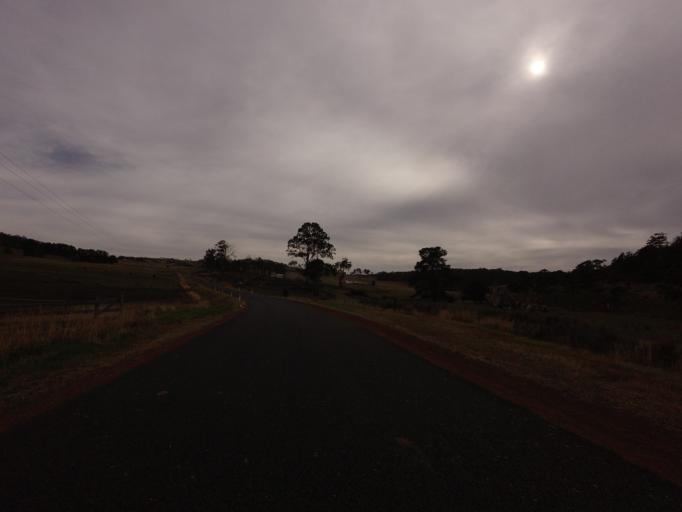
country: AU
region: Tasmania
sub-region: Sorell
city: Sorell
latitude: -42.4617
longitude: 147.5727
